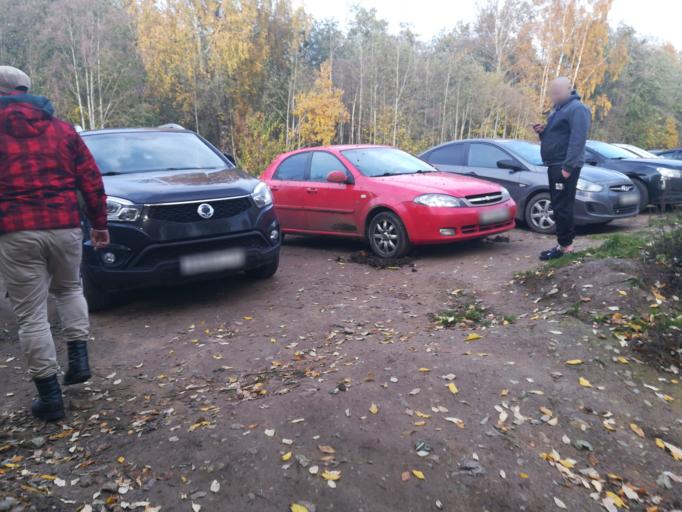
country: RU
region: Leningrad
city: Sista-Palkino
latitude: 59.5927
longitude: 28.8283
